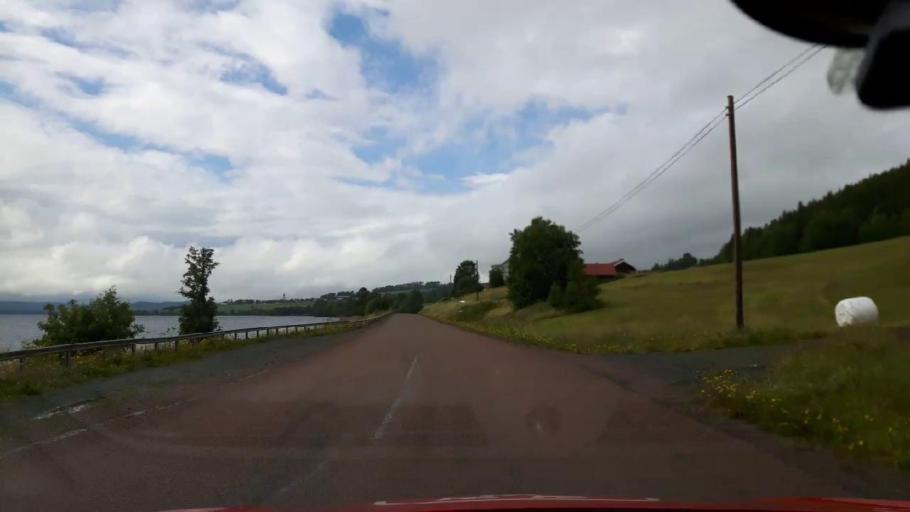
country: SE
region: Jaemtland
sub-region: Krokoms Kommun
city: Valla
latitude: 63.3831
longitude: 13.9915
